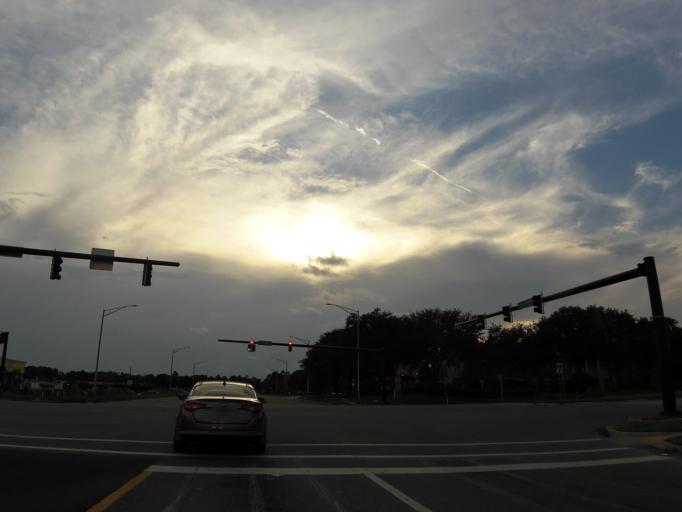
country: US
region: Florida
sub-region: Duval County
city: Jacksonville
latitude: 30.2478
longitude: -81.5356
